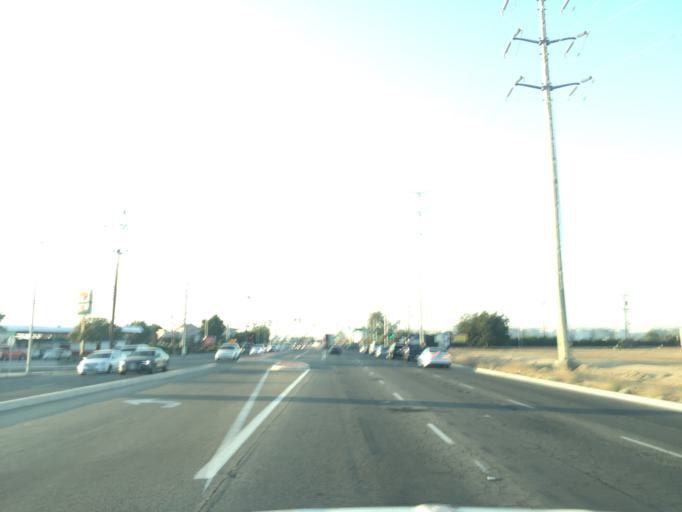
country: US
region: California
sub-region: Fresno County
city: Sunnyside
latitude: 36.7489
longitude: -119.7001
